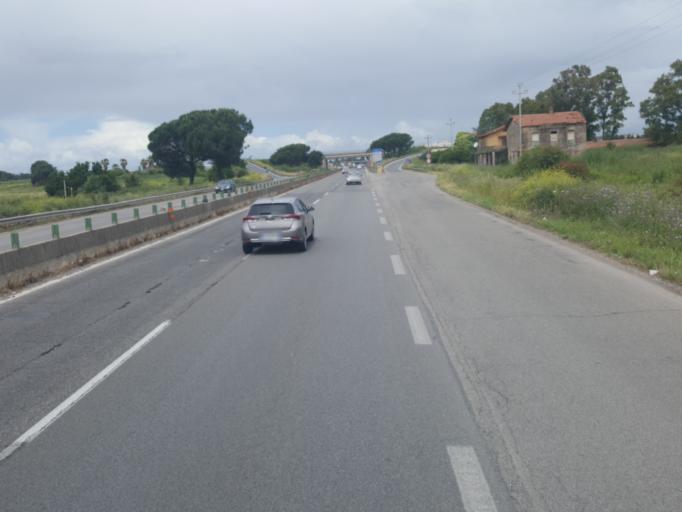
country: IT
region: Latium
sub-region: Provincia di Latina
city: Aprilia
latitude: 41.5704
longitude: 12.6668
